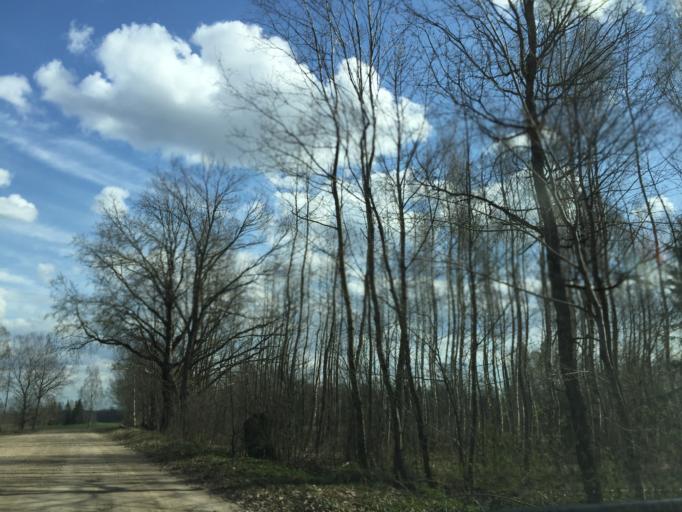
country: LV
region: Skriveri
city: Skriveri
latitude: 56.7989
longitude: 25.1402
